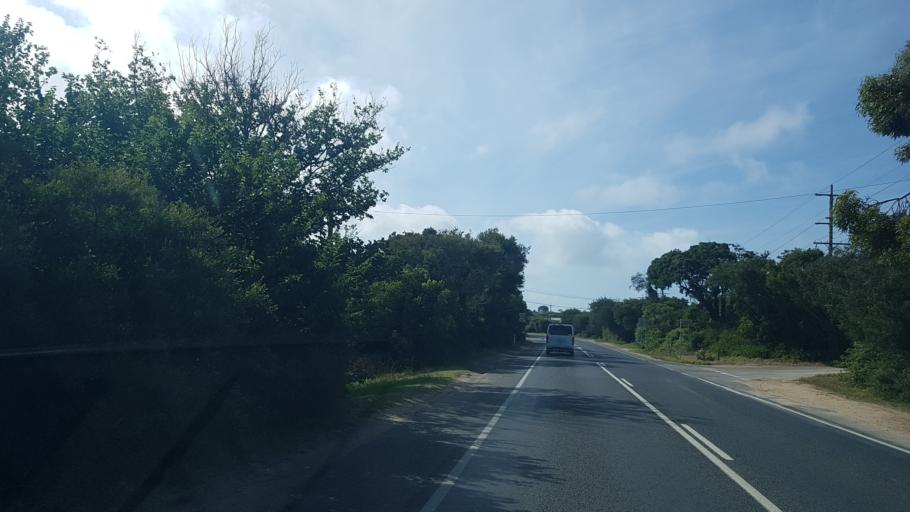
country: AU
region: Victoria
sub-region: Mornington Peninsula
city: Blairgowrie
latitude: -38.3612
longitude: 144.7607
